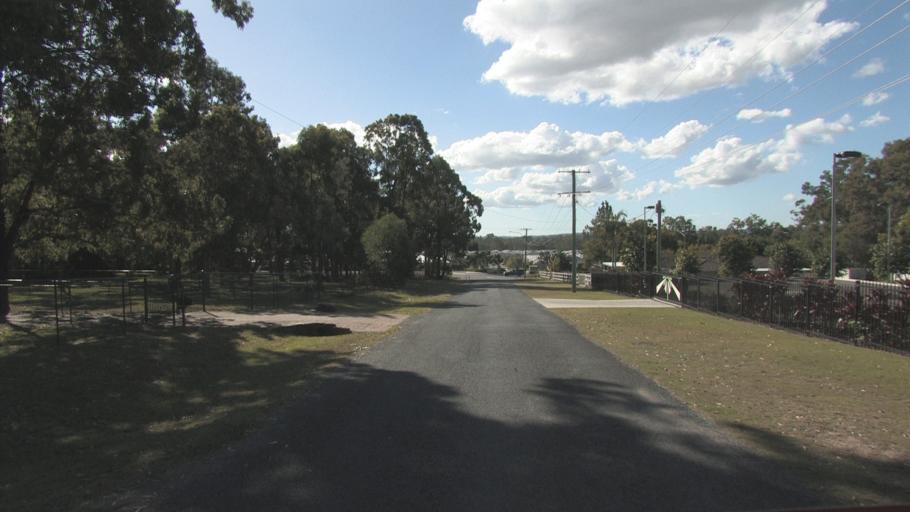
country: AU
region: Queensland
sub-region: Logan
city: Logan Reserve
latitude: -27.7146
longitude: 153.1112
